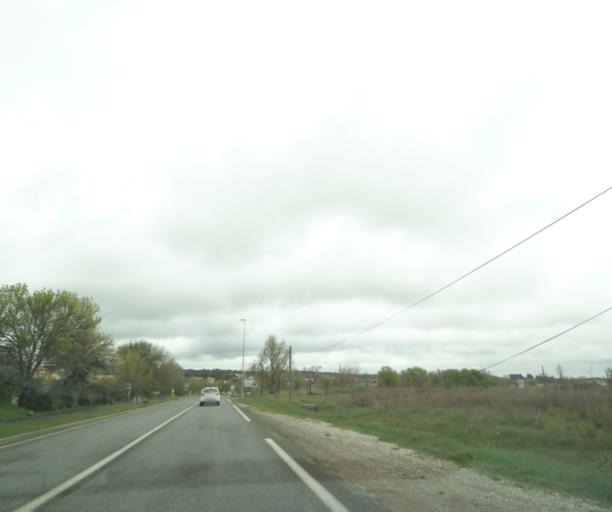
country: FR
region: Languedoc-Roussillon
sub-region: Departement de l'Herault
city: Cournonterral
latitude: 43.5585
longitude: 3.7288
